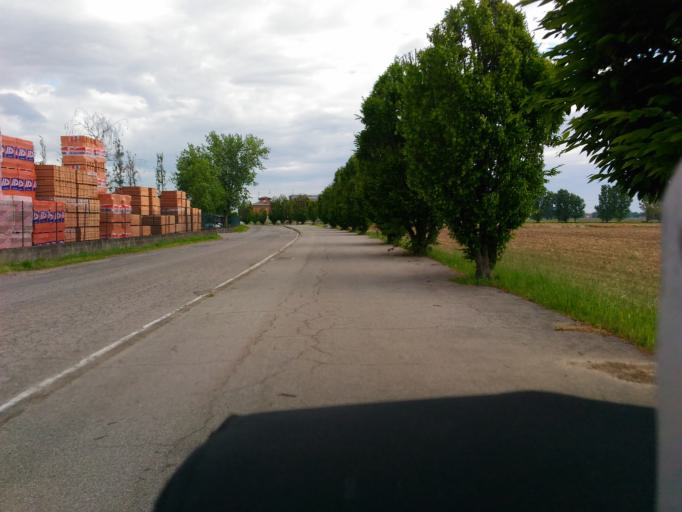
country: IT
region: Lombardy
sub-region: Citta metropolitana di Milano
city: Vizzolo Predabissi
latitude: 45.3547
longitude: 9.3523
